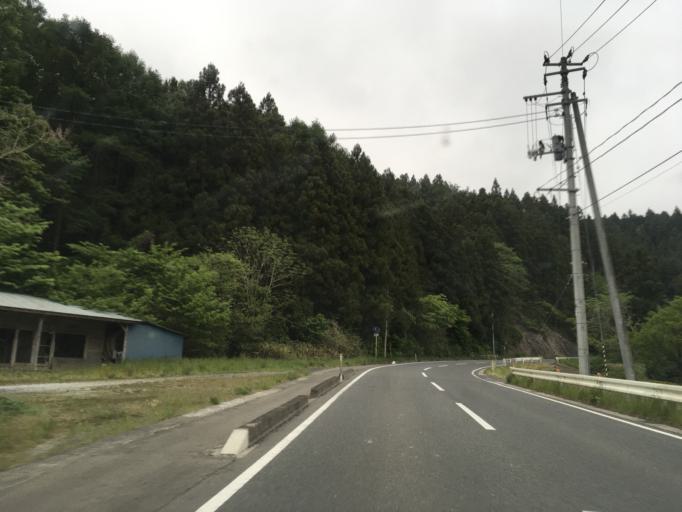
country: JP
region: Iwate
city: Ichinoseki
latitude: 38.7337
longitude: 141.3035
